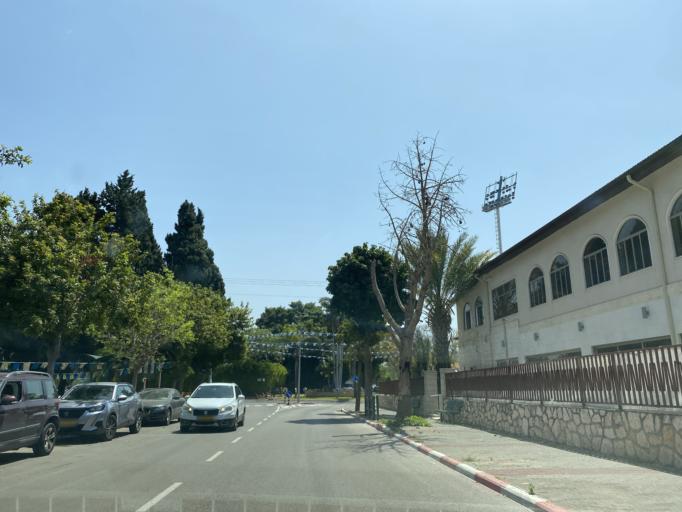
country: IL
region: Central District
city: Ra'anana
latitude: 32.1875
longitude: 34.8715
